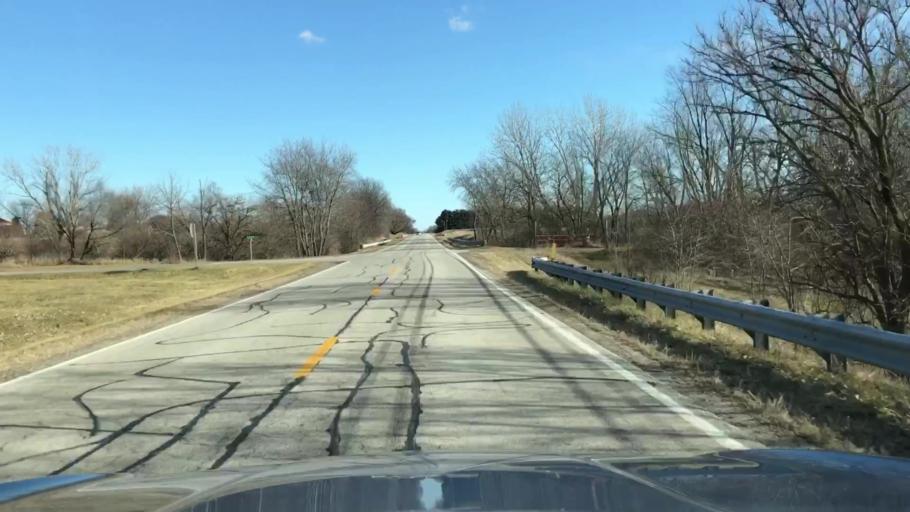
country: US
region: Illinois
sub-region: McLean County
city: Lexington
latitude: 40.6483
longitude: -88.8590
